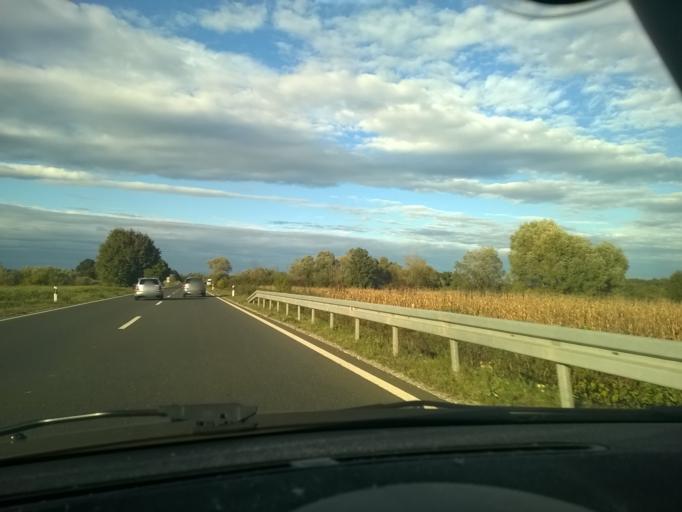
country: HR
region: Zagrebacka
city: Pojatno
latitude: 45.9179
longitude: 15.8196
